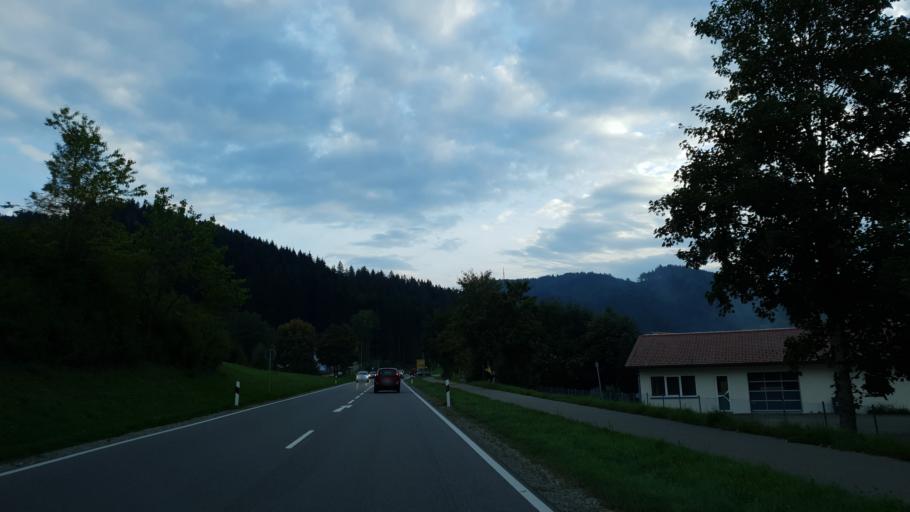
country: DE
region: Bavaria
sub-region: Swabia
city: Maierhofen
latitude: 47.6579
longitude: 10.0898
